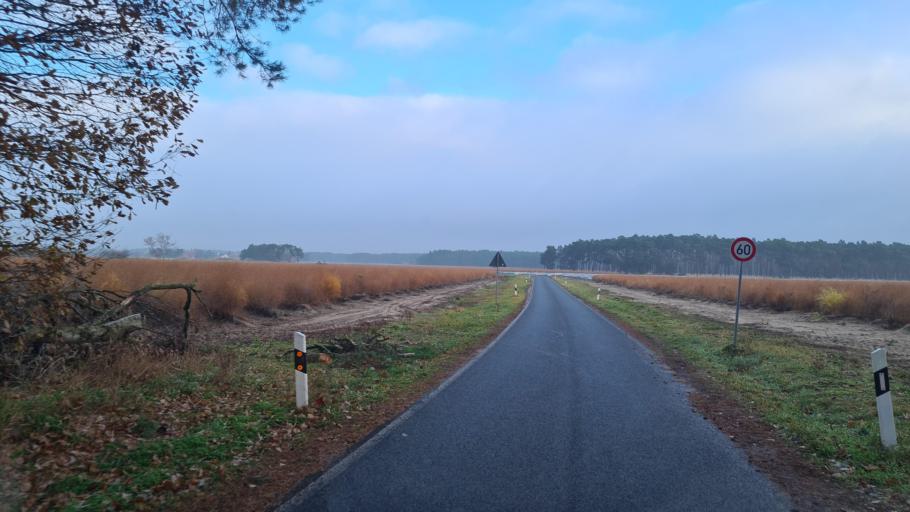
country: DE
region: Brandenburg
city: Beelitz
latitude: 52.1451
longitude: 12.9637
